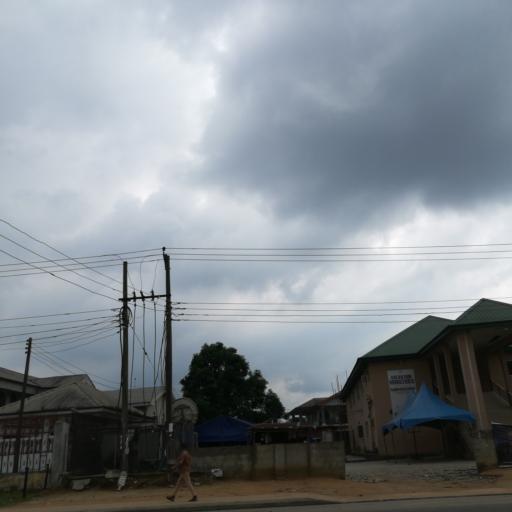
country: NG
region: Rivers
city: Port Harcourt
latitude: 4.8355
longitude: 7.0702
